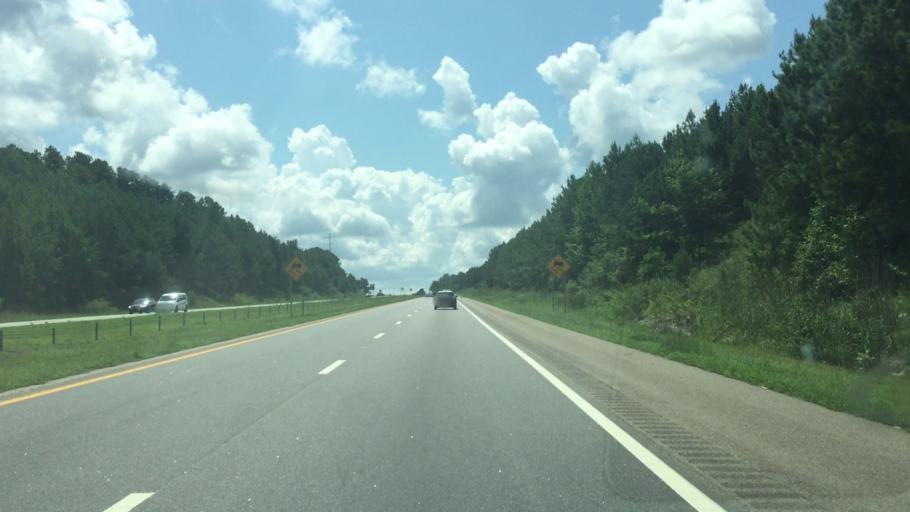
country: US
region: North Carolina
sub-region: Richmond County
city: Cordova
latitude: 34.9425
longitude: -79.8445
